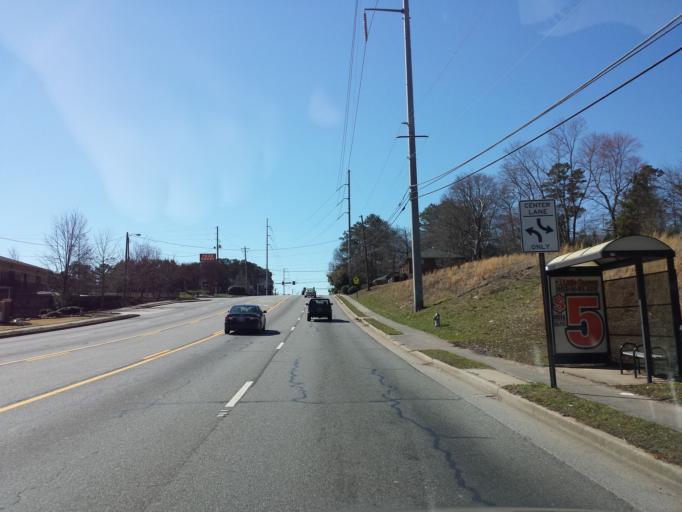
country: US
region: Georgia
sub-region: Cobb County
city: Fair Oaks
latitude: 33.8948
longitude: -84.5507
